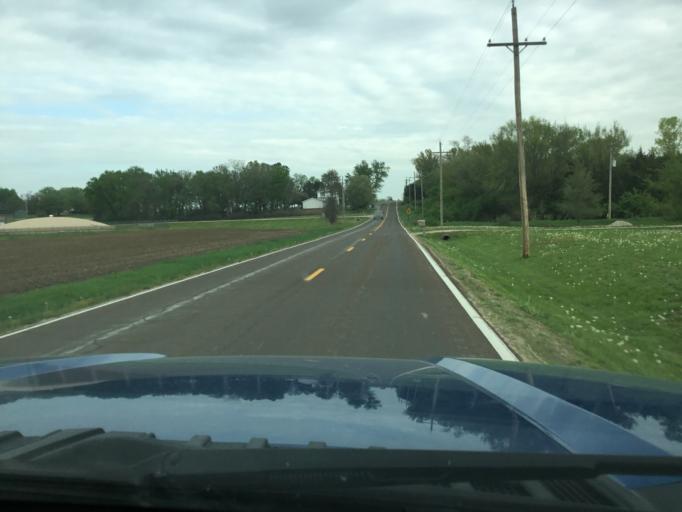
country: US
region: Kansas
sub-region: Shawnee County
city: Topeka
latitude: 39.1029
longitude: -95.7484
